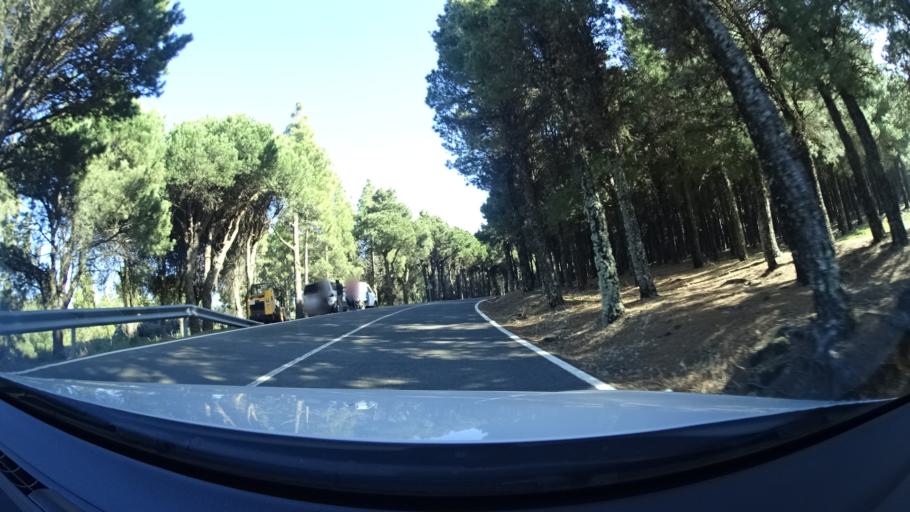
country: ES
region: Canary Islands
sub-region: Provincia de Las Palmas
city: Vega de San Mateo
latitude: 27.9659
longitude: -15.5472
